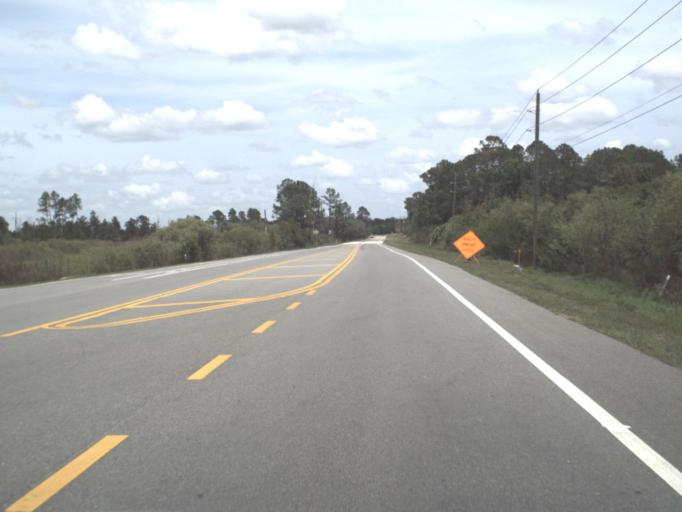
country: US
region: Florida
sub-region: Lake County
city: Lake Mack-Forest Hills
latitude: 28.9191
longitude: -81.4446
